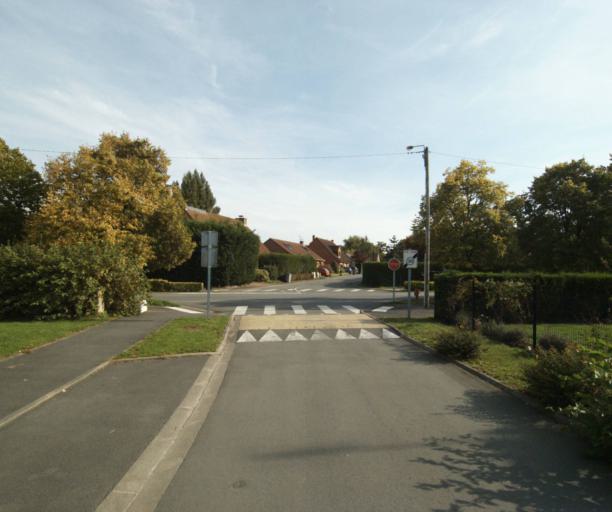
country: FR
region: Nord-Pas-de-Calais
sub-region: Departement du Nord
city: Fournes-en-Weppes
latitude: 50.5883
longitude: 2.8906
